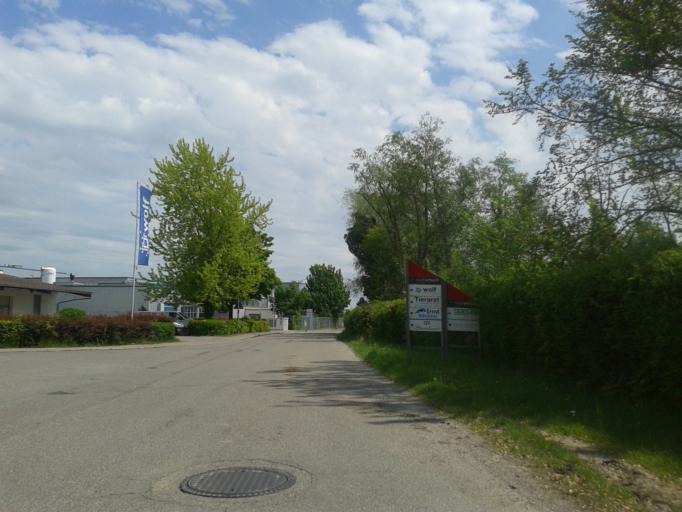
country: DE
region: Baden-Wuerttemberg
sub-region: Tuebingen Region
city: Erbach
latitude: 48.3245
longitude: 9.8993
